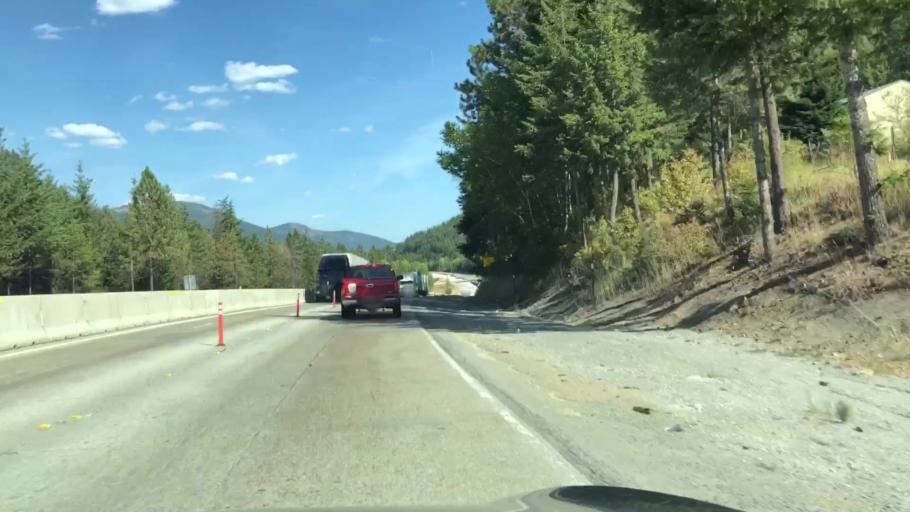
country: US
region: Idaho
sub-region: Shoshone County
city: Wallace
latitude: 47.4690
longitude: -115.7940
